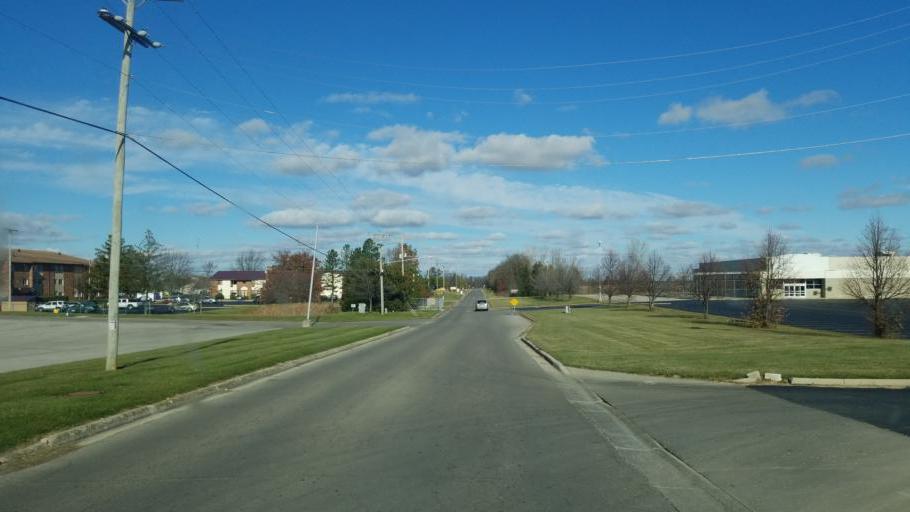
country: US
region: Ohio
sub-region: Hardin County
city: Kenton
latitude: 40.6530
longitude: -83.5906
